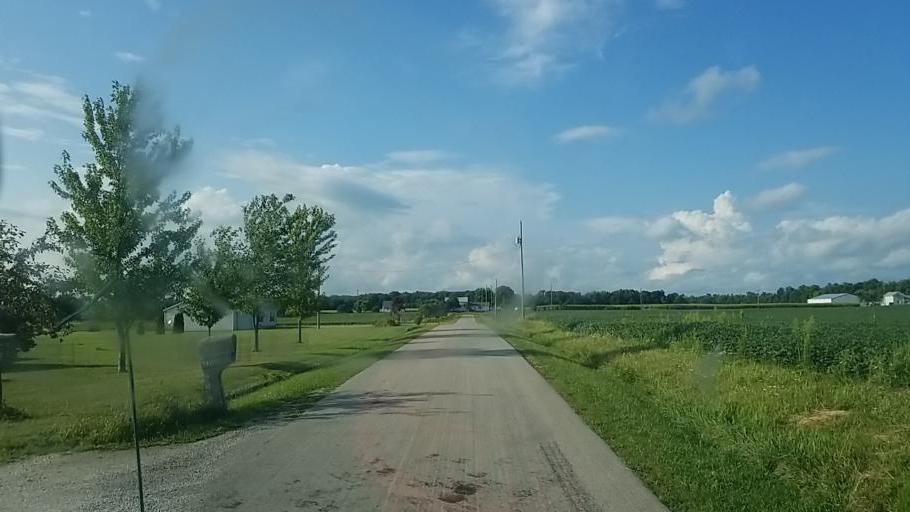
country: US
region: Ohio
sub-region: Wyandot County
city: Upper Sandusky
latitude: 40.8379
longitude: -83.1602
